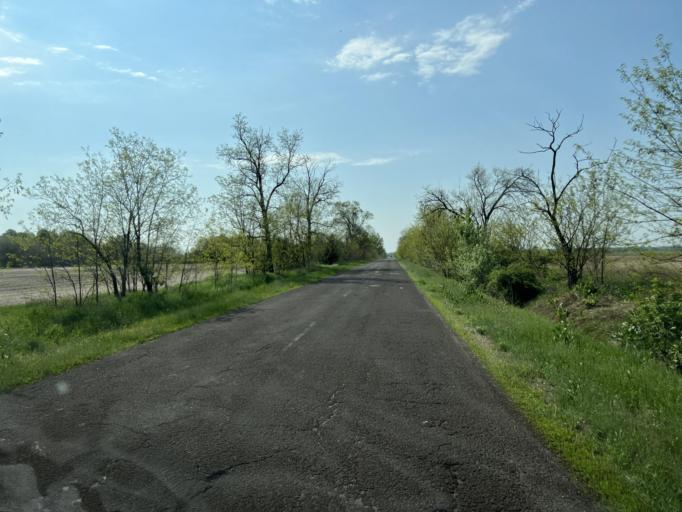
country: HU
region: Pest
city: Jaszkarajeno
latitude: 47.0202
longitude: 20.0410
